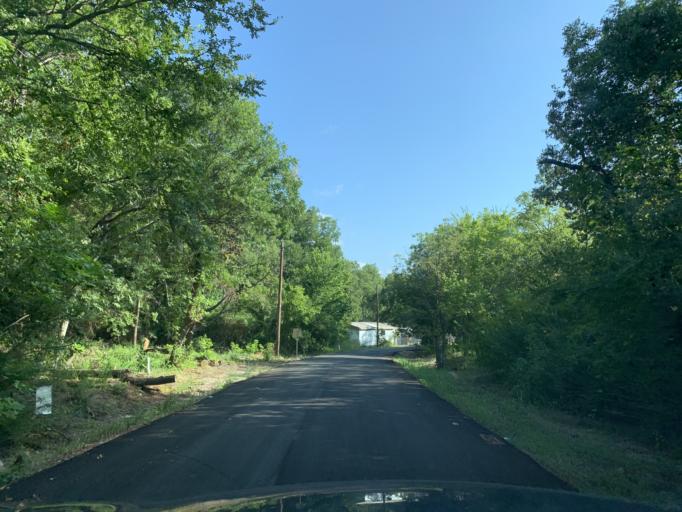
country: US
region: Texas
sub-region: Dallas County
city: Hutchins
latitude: 32.6744
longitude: -96.7820
